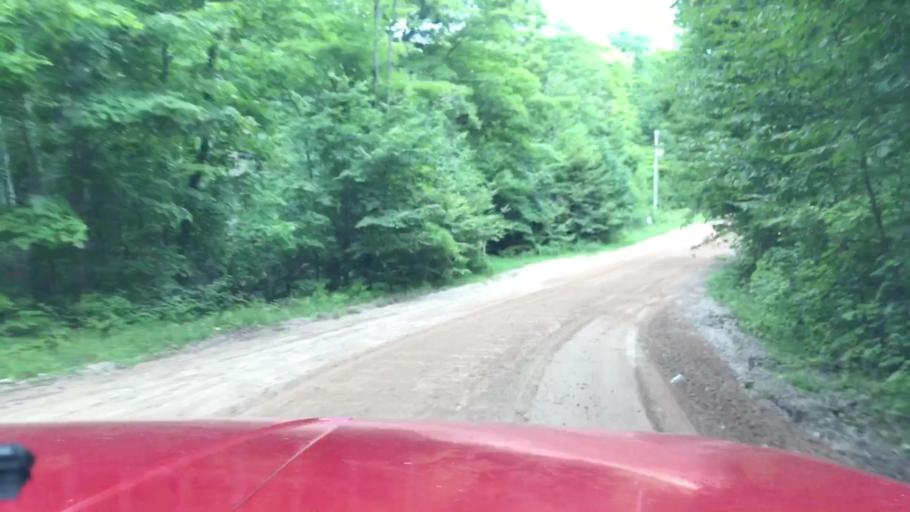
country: US
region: Michigan
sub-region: Charlevoix County
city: Charlevoix
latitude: 45.7273
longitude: -85.5664
